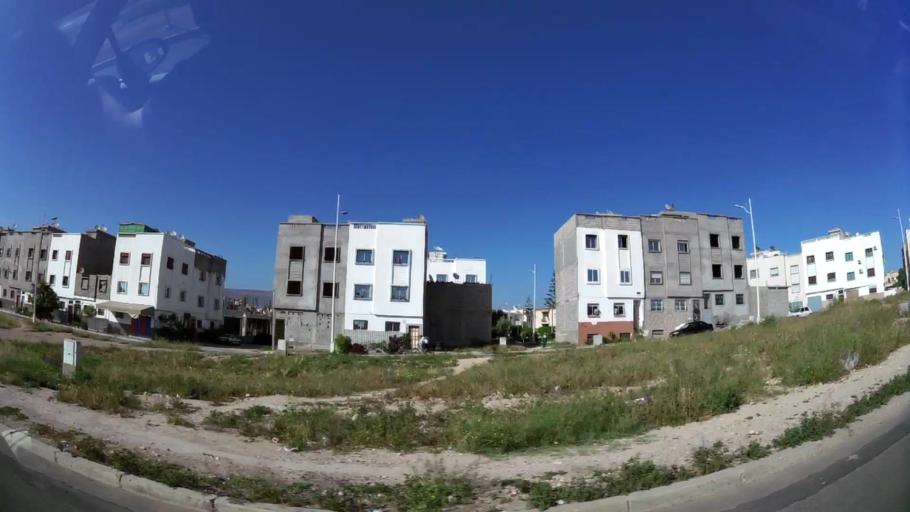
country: MA
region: Souss-Massa-Draa
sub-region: Agadir-Ida-ou-Tnan
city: Agadir
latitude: 30.4254
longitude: -9.5749
